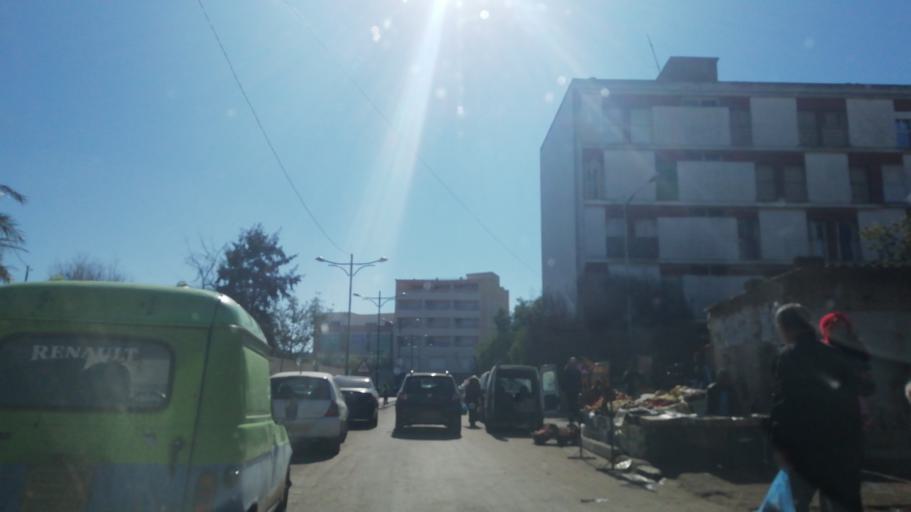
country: DZ
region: Oran
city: Es Senia
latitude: 35.6506
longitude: -0.6213
